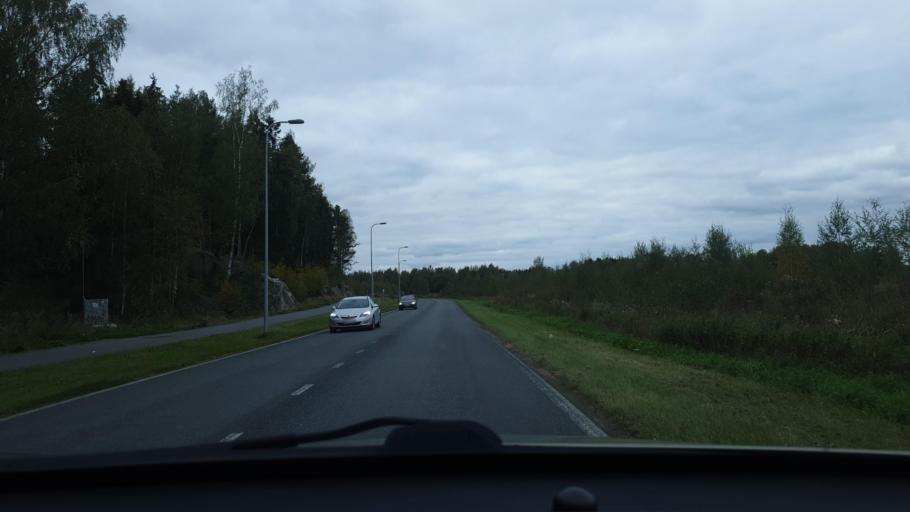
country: FI
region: Ostrobothnia
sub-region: Vaasa
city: Teeriniemi
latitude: 63.0986
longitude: 21.6976
